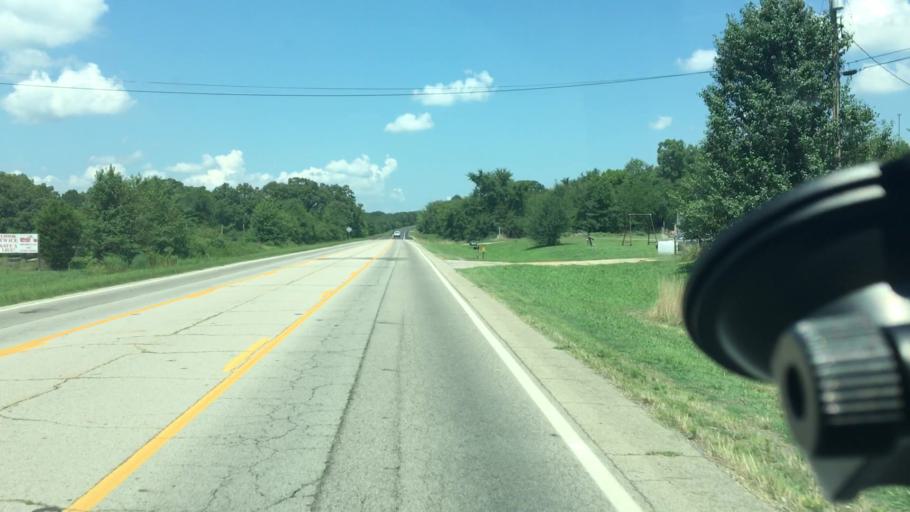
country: US
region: Arkansas
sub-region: Sebastian County
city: Lavaca
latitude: 35.2966
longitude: -94.1483
